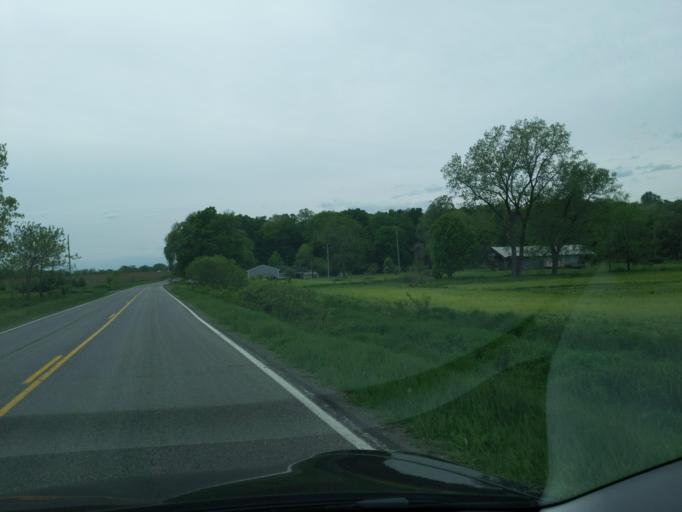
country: US
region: Michigan
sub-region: Ingham County
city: Leslie
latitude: 42.4479
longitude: -84.3613
